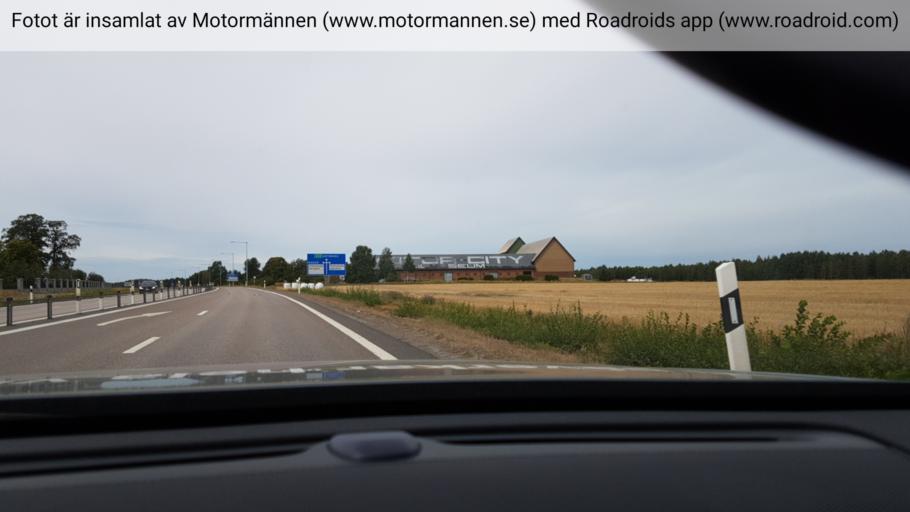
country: SE
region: Vaestra Goetaland
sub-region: Skara Kommun
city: Skara
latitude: 58.3724
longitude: 13.3892
